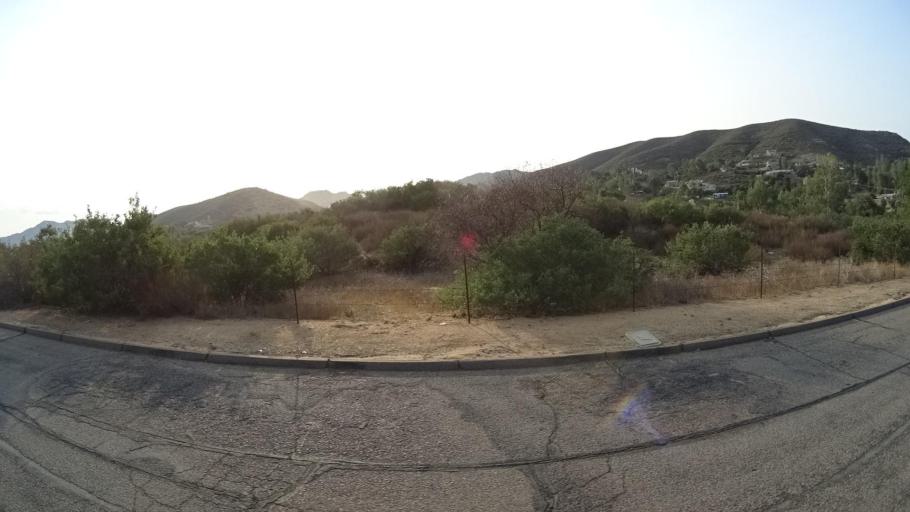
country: US
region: California
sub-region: San Diego County
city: Ramona
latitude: 32.9946
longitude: -116.8485
